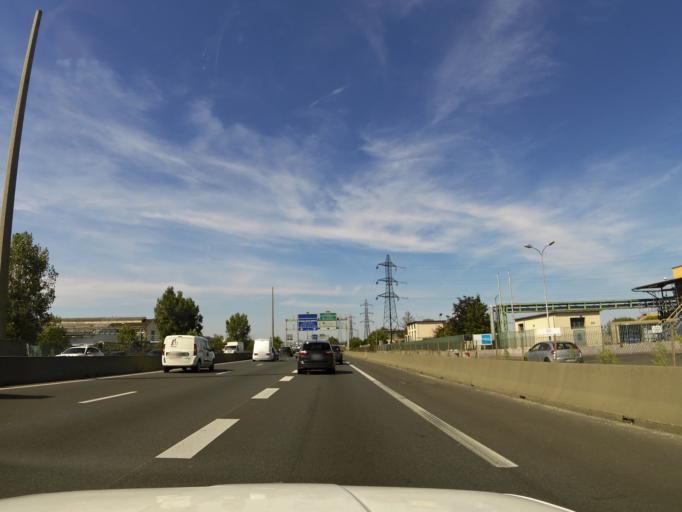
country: FR
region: Rhone-Alpes
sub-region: Departement du Rhone
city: Feyzin
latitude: 45.6880
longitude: 4.8464
